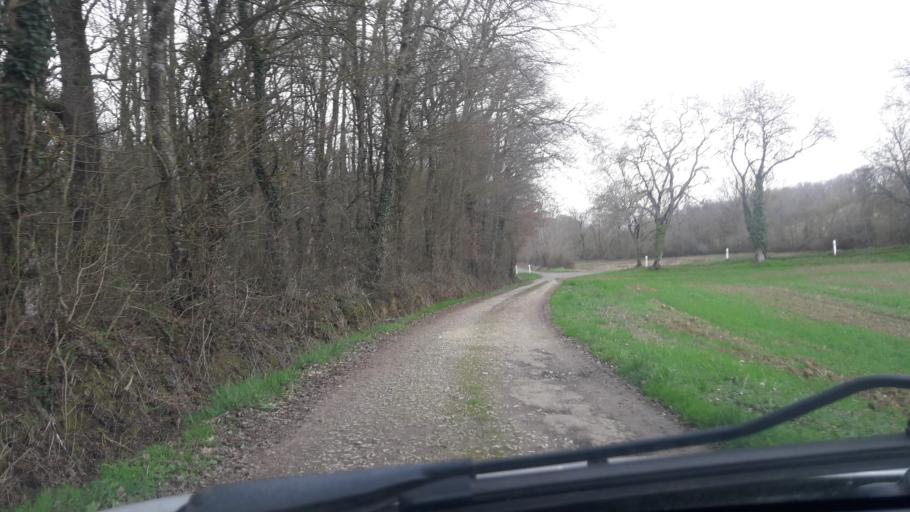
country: FR
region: Midi-Pyrenees
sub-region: Departement du Gers
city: Gimont
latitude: 43.6553
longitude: 0.9763
